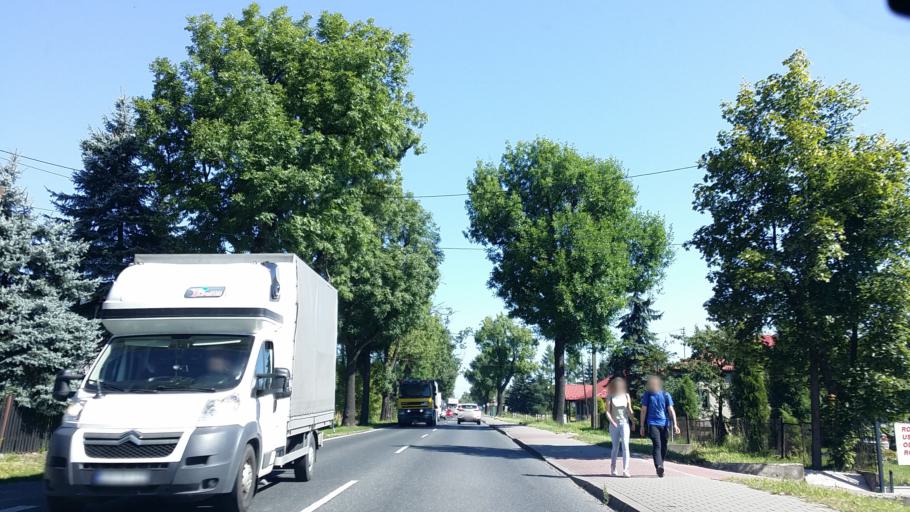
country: PL
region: Silesian Voivodeship
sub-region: Powiat bierunsko-ledzinski
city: Chelm Slaski
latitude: 50.0831
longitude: 19.1973
